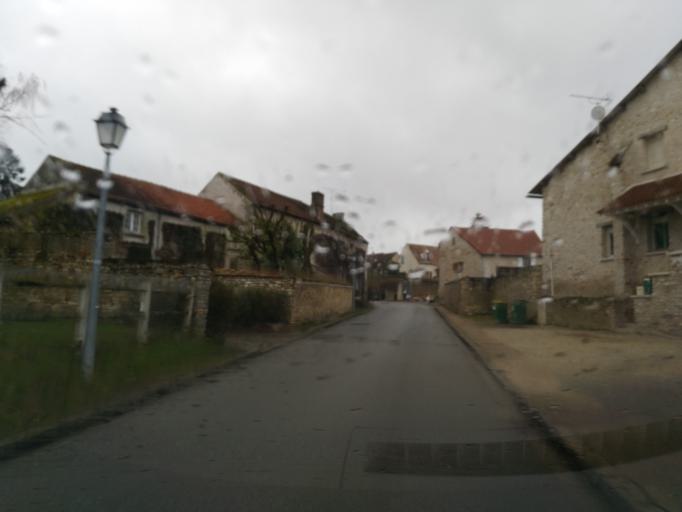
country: FR
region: Ile-de-France
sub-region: Departement des Yvelines
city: Thoiry
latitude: 48.8630
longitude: 1.8143
